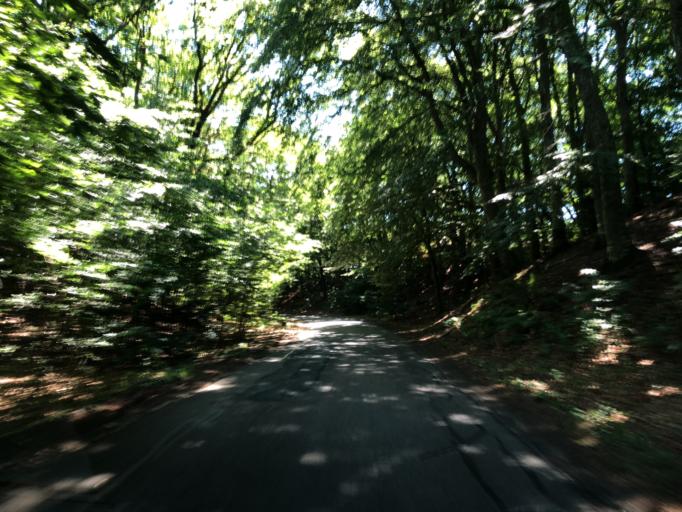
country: DK
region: Central Jutland
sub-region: Viborg Kommune
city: Viborg
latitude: 56.5156
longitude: 9.4953
